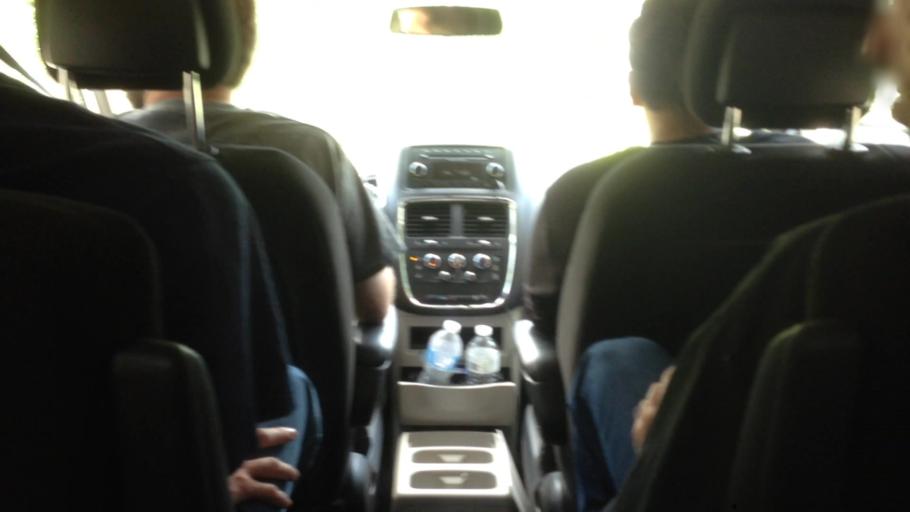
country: US
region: New York
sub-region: Dutchess County
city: Red Hook
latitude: 42.0111
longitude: -73.9161
